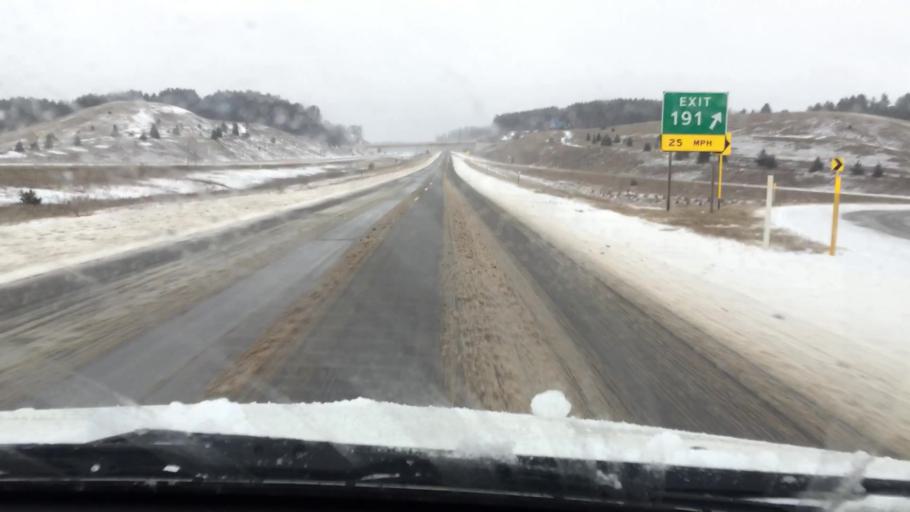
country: US
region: Michigan
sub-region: Wexford County
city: Manton
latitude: 44.4047
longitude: -85.3810
